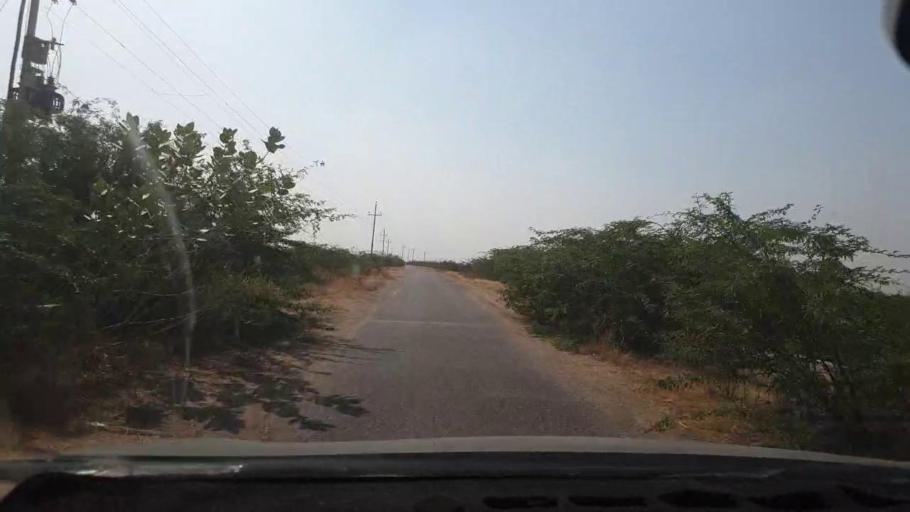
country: PK
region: Sindh
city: Malir Cantonment
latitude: 25.1103
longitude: 67.2043
